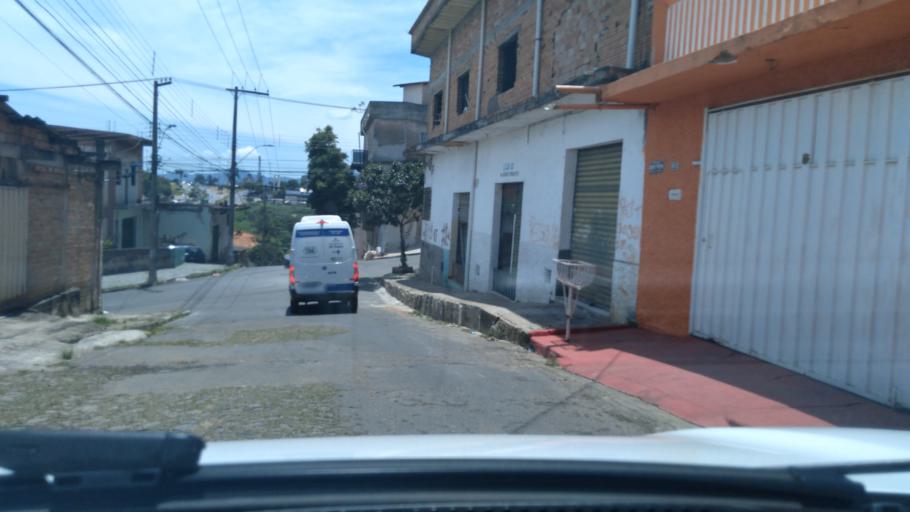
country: BR
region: Minas Gerais
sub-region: Contagem
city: Contagem
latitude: -19.9255
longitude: -44.0136
